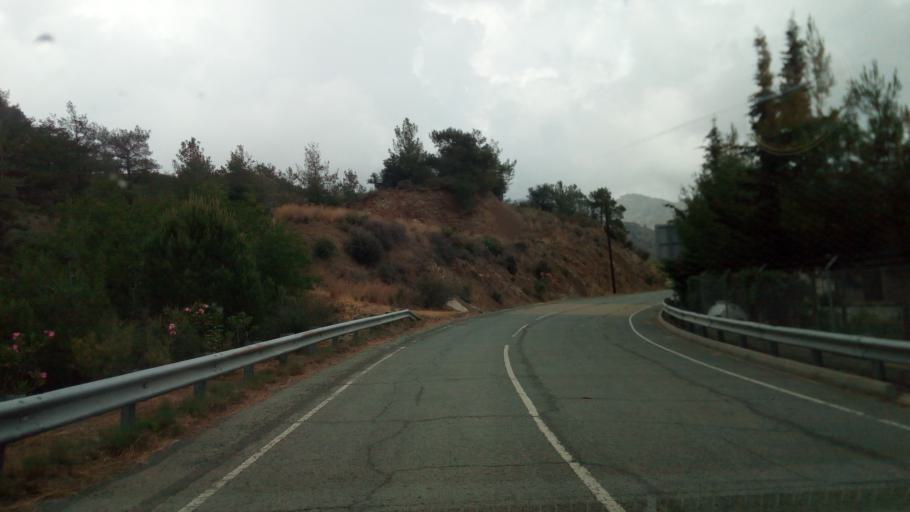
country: CY
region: Limassol
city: Parekklisha
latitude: 34.8649
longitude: 33.1870
